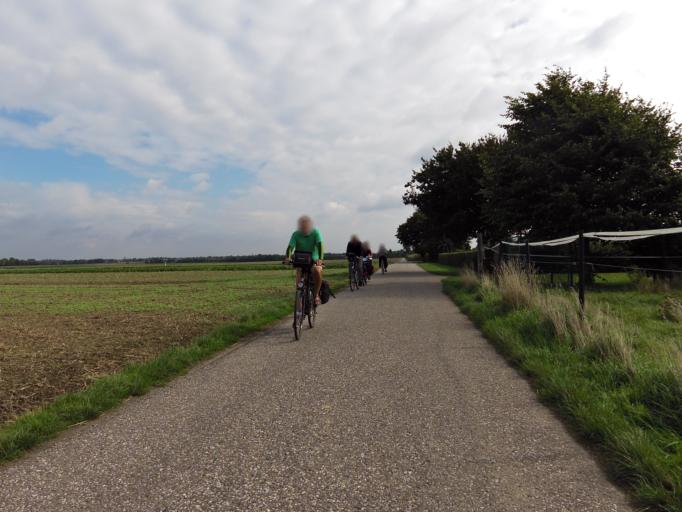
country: DE
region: North Rhine-Westphalia
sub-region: Regierungsbezirk Koln
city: Ubach-Palenberg
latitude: 50.9325
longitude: 6.0686
